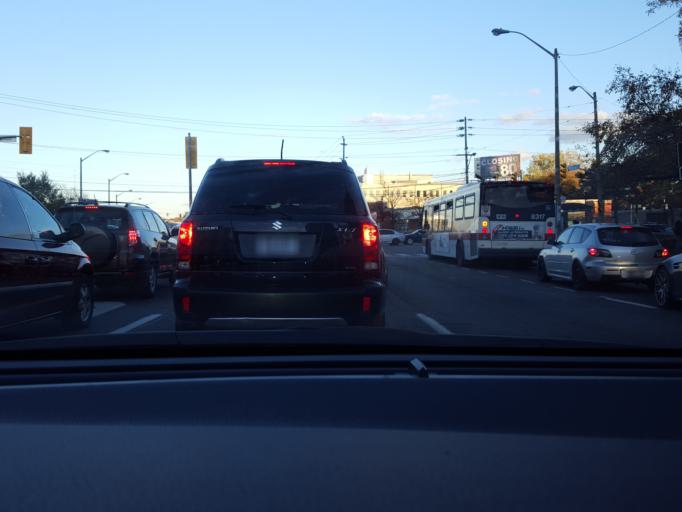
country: CA
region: Ontario
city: Willowdale
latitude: 43.7528
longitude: -79.3607
